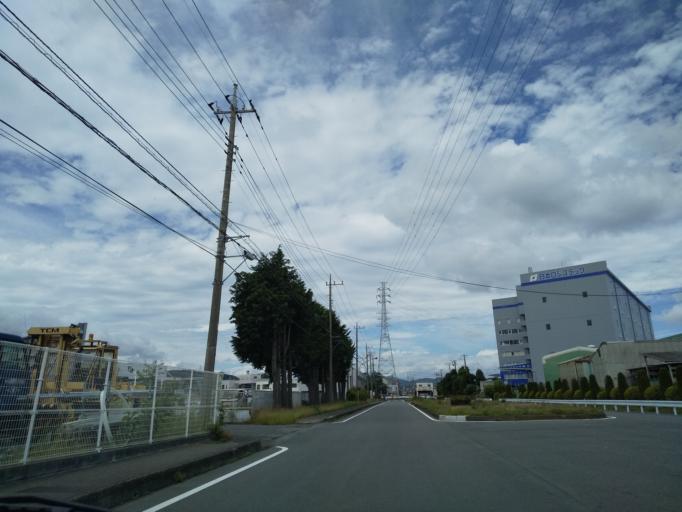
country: JP
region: Kanagawa
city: Zama
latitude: 35.5106
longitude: 139.3436
